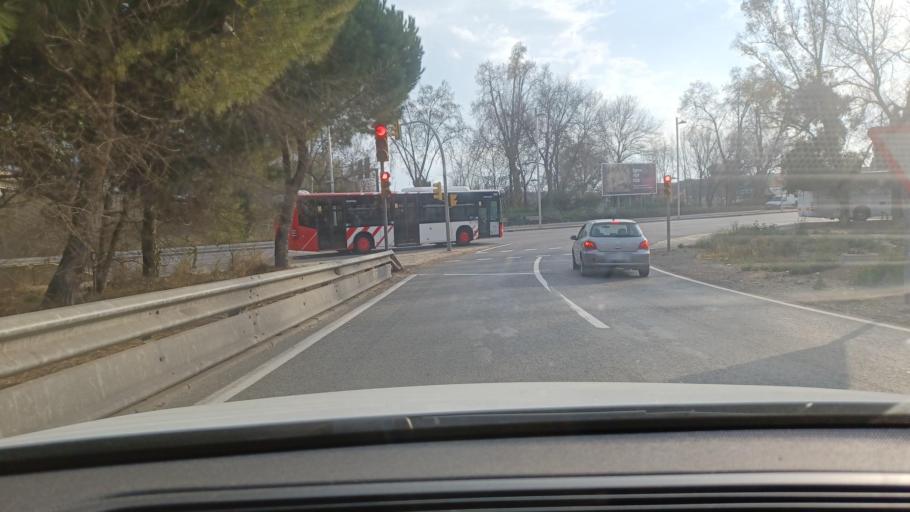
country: ES
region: Catalonia
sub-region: Provincia de Tarragona
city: Tarragona
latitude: 41.1163
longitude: 1.2270
